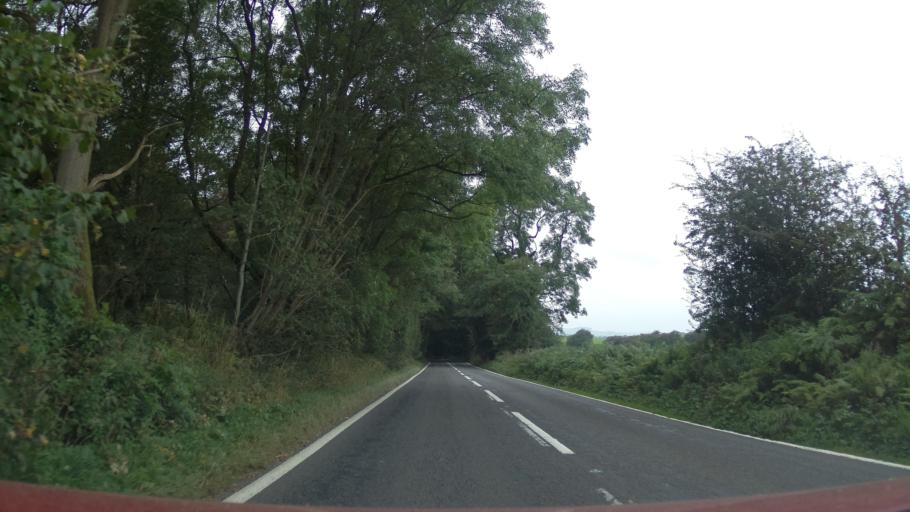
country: GB
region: England
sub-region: Derbyshire
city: Bradley
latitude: 53.0136
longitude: -1.6996
